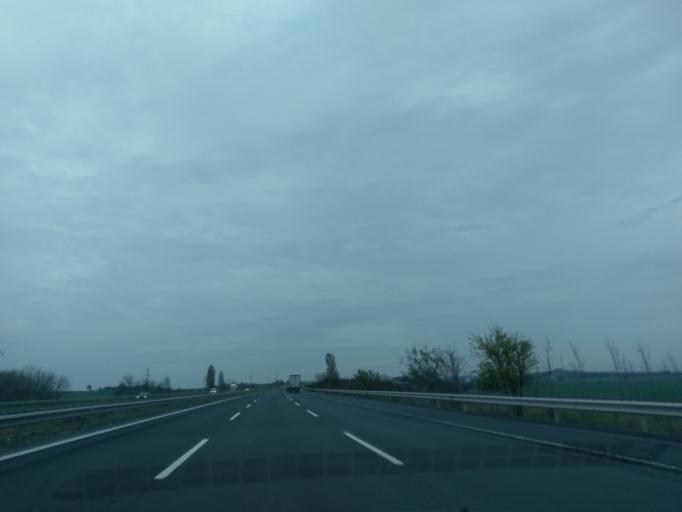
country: TR
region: Istanbul
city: Canta
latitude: 41.1342
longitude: 28.1546
